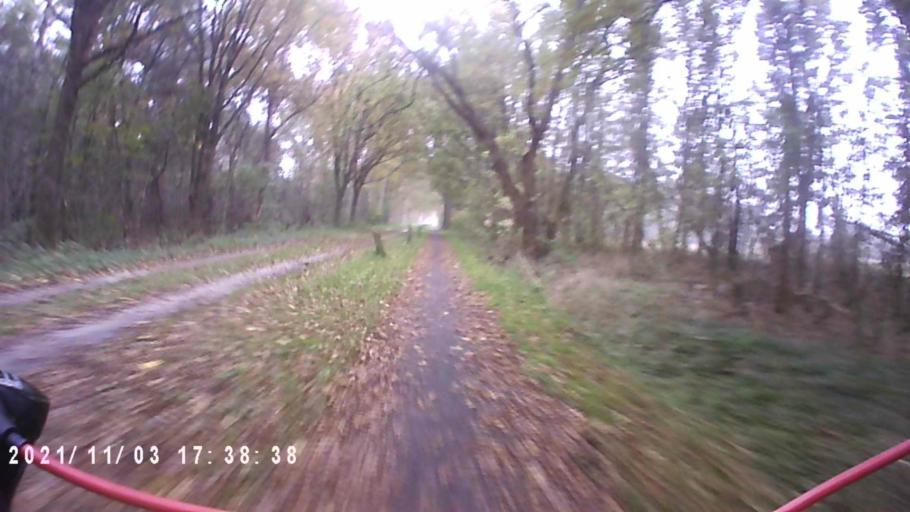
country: NL
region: Drenthe
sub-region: Gemeente Westerveld
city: Dwingeloo
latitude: 52.8693
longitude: 6.2908
